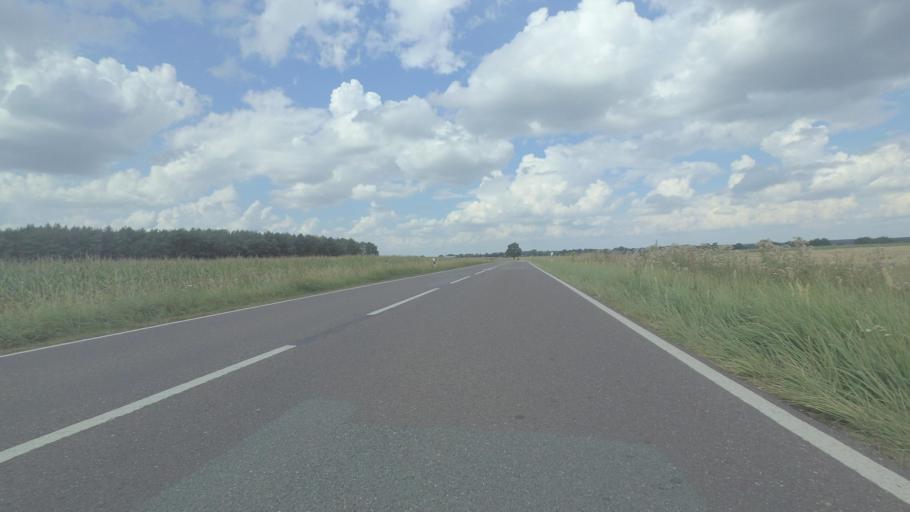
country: DE
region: Brandenburg
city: Wittstock
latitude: 53.2295
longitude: 12.4351
